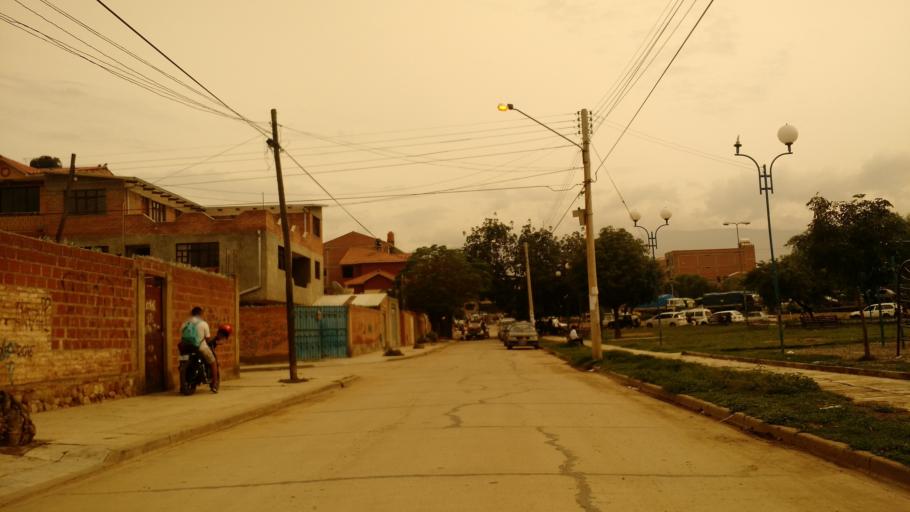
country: BO
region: Cochabamba
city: Cochabamba
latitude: -17.4305
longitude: -66.1560
